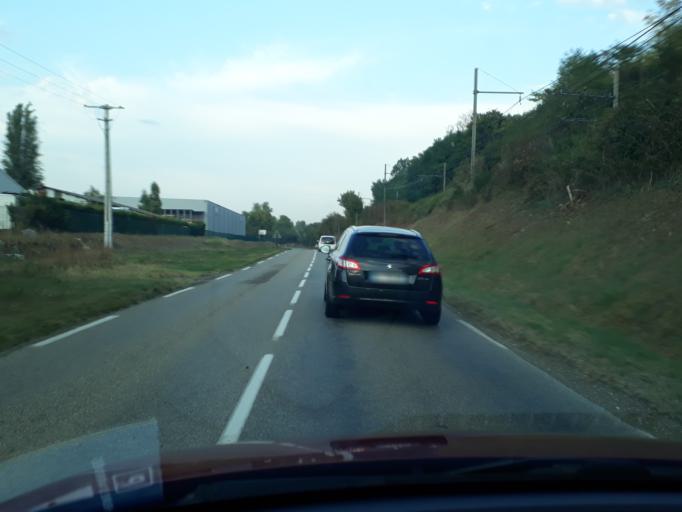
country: FR
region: Rhone-Alpes
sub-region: Departement du Rhone
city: Ampuis
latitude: 45.4848
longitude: 4.8191
